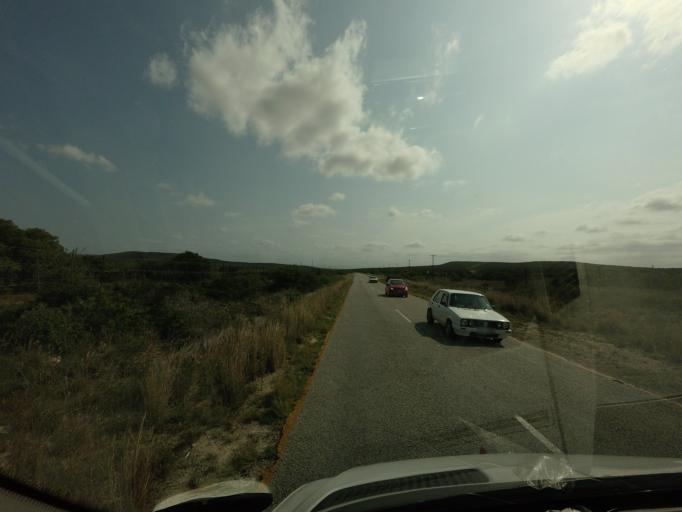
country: ZA
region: Eastern Cape
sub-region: Nelson Mandela Bay Metropolitan Municipality
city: Uitenhage
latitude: -33.6282
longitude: 25.6037
